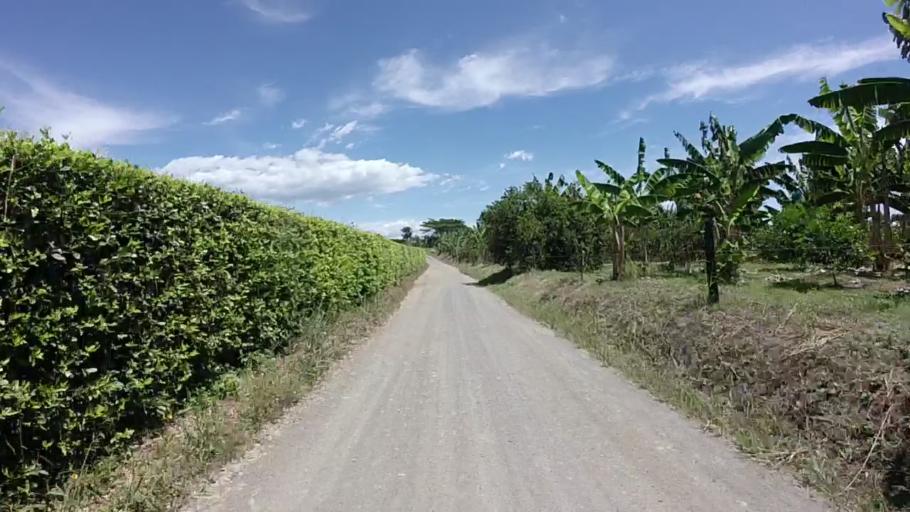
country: CO
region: Valle del Cauca
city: Alcala
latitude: 4.7067
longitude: -75.8171
